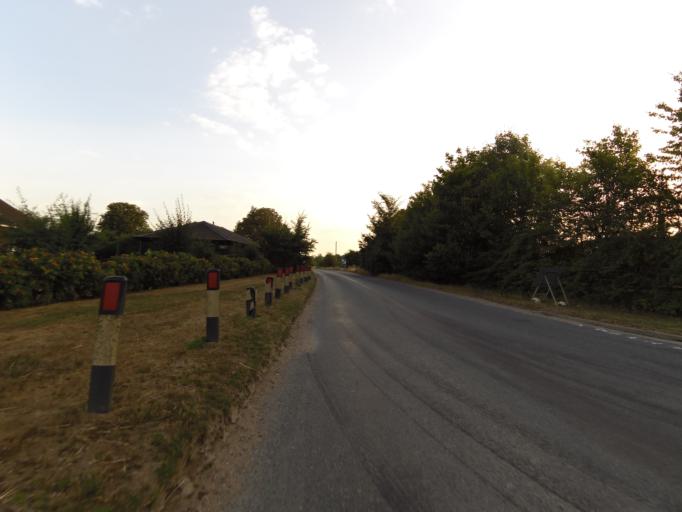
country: GB
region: England
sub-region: Suffolk
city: Bramford
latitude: 52.1001
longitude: 1.1065
